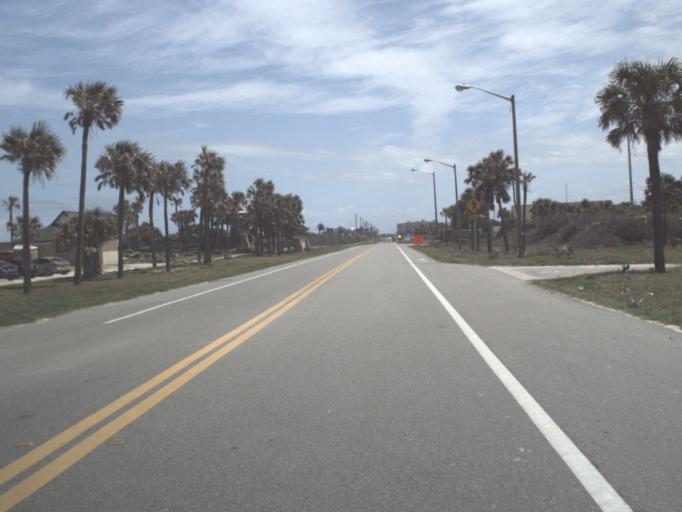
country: US
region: Florida
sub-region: Flagler County
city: Palm Coast
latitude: 29.6660
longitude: -81.2122
